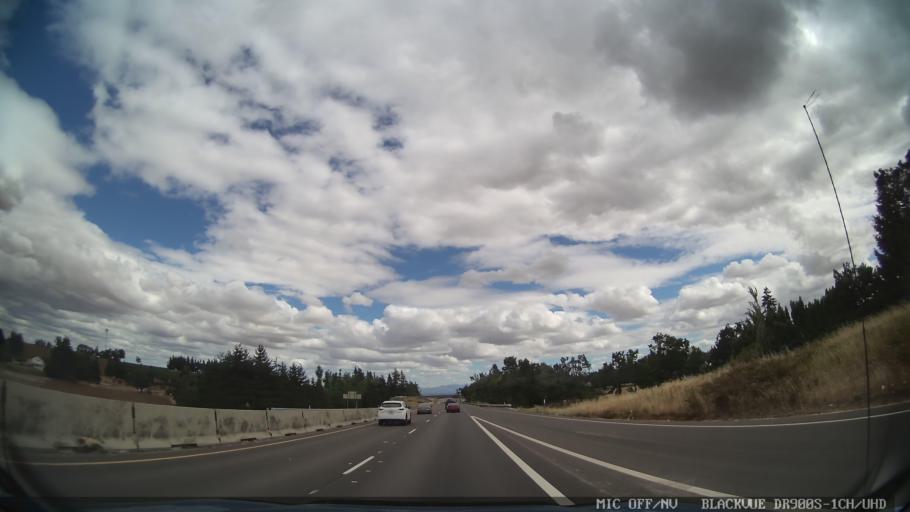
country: US
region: Oregon
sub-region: Marion County
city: Turner
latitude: 44.8830
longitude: -122.9173
